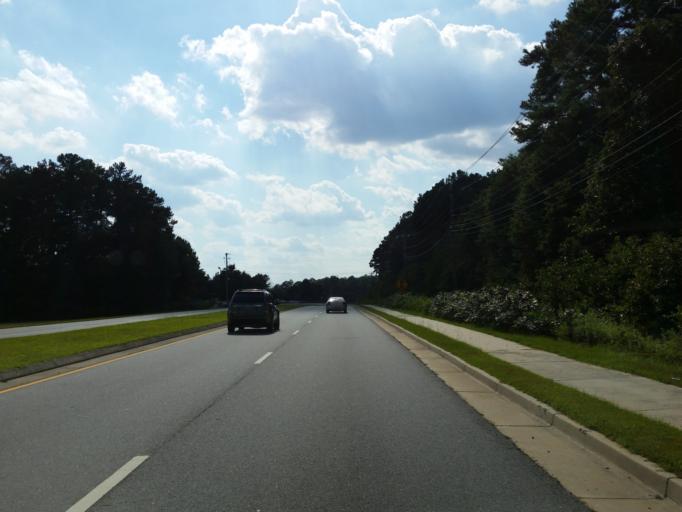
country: US
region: Georgia
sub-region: Gwinnett County
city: Lawrenceville
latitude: 33.9514
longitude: -84.0626
